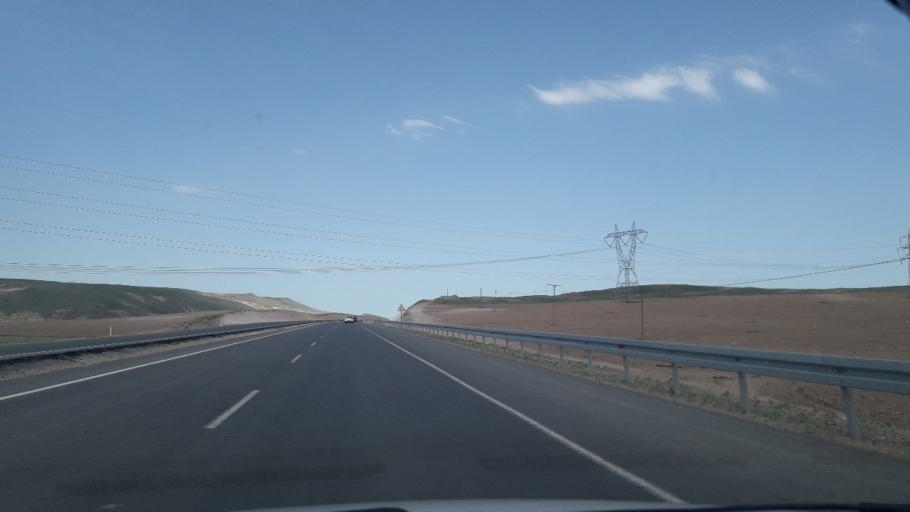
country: TR
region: Sivas
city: Deliktas
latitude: 39.2031
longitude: 37.2265
